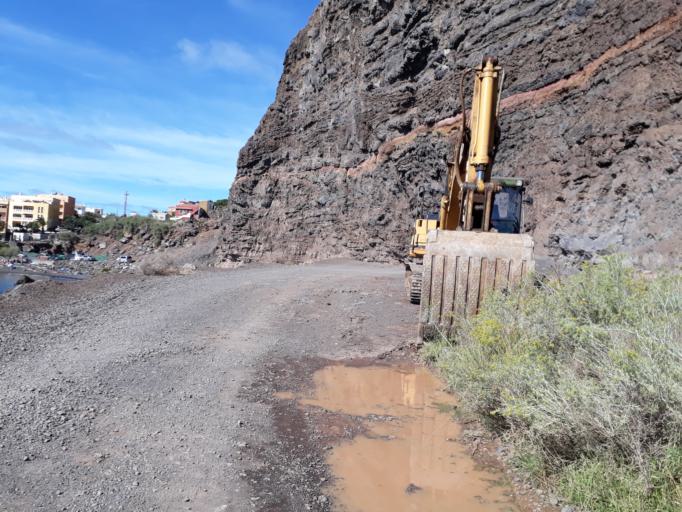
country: ES
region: Canary Islands
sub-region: Provincia de Santa Cruz de Tenerife
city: Alajero
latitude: 28.0818
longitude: -17.3304
